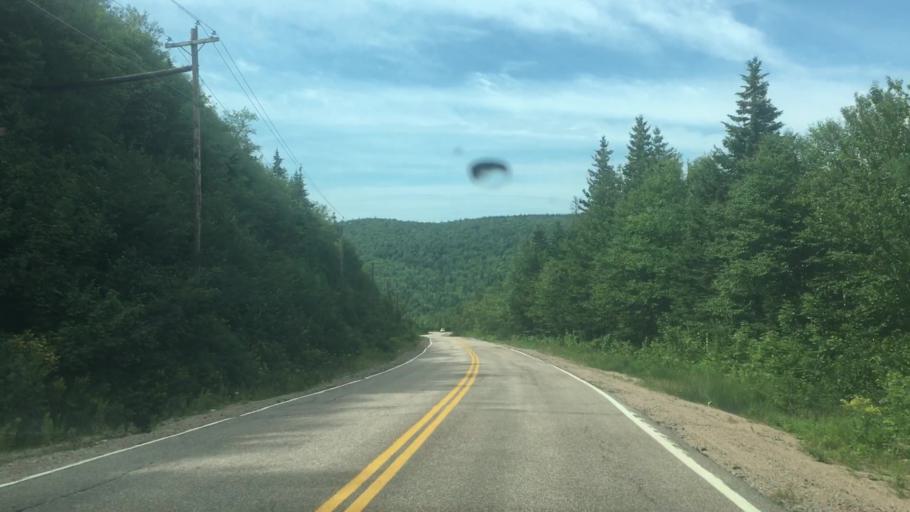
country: CA
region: Nova Scotia
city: Sydney Mines
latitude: 46.6040
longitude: -60.3869
